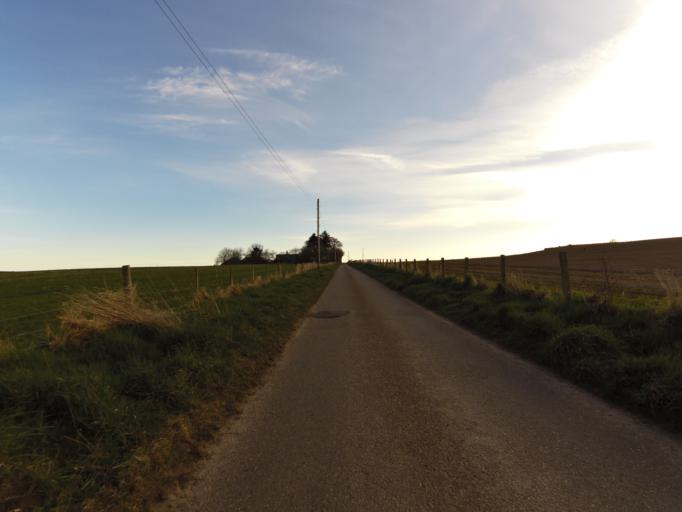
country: GB
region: Scotland
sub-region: Aberdeenshire
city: Stonehaven
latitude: 56.9384
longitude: -2.2227
